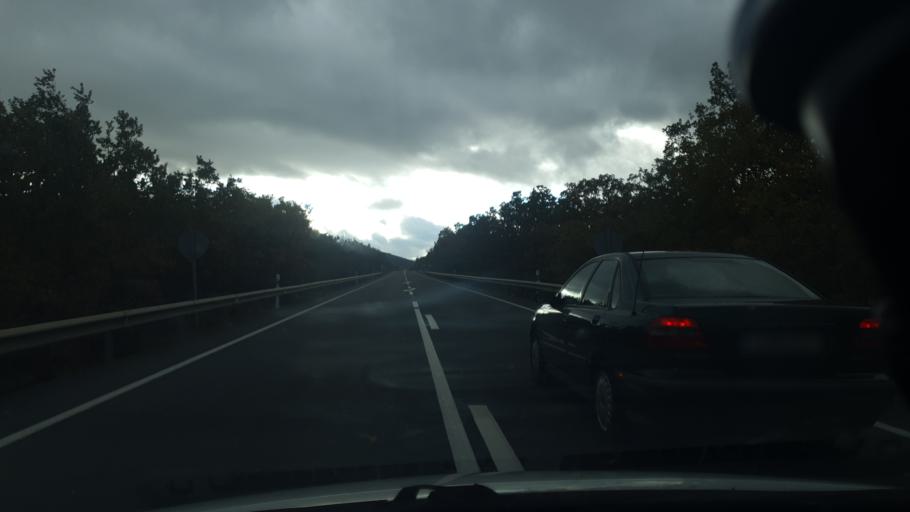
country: ES
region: Castille and Leon
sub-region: Provincia de Segovia
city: Villacastin
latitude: 40.7567
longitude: -4.4465
